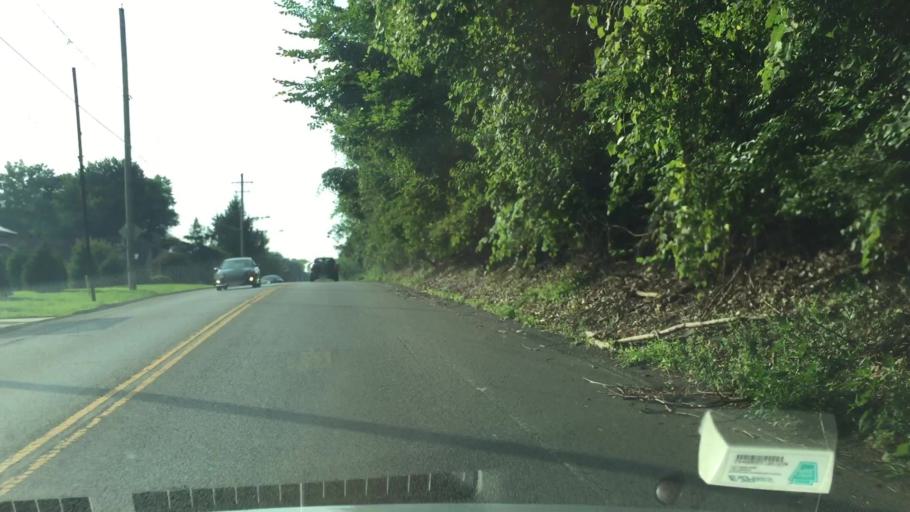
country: US
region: Pennsylvania
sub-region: Allegheny County
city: Heidelberg
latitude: 40.3718
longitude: -80.0891
